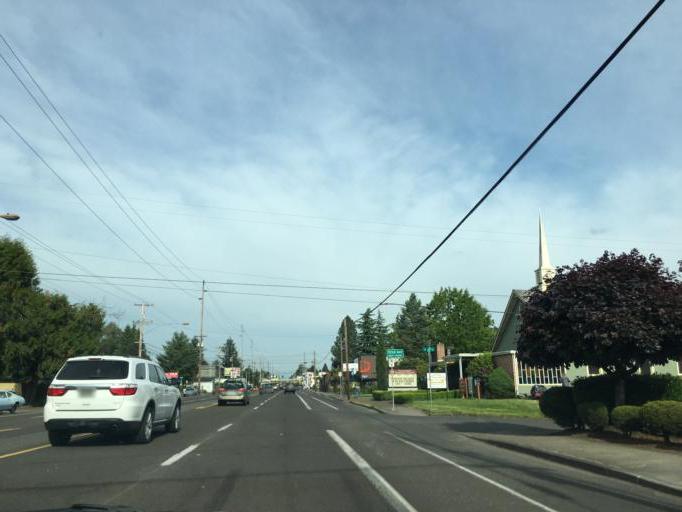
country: US
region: Oregon
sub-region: Multnomah County
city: Lents
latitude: 45.5045
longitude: -122.5721
